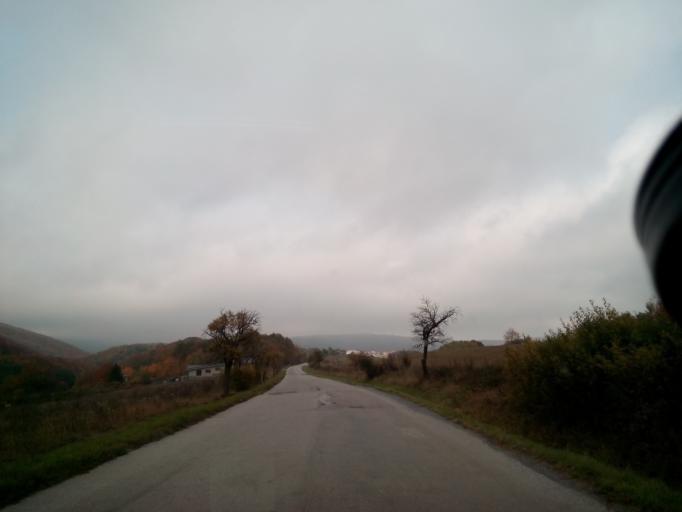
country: SK
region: Kosicky
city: Kosice
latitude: 48.7304
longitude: 21.1344
